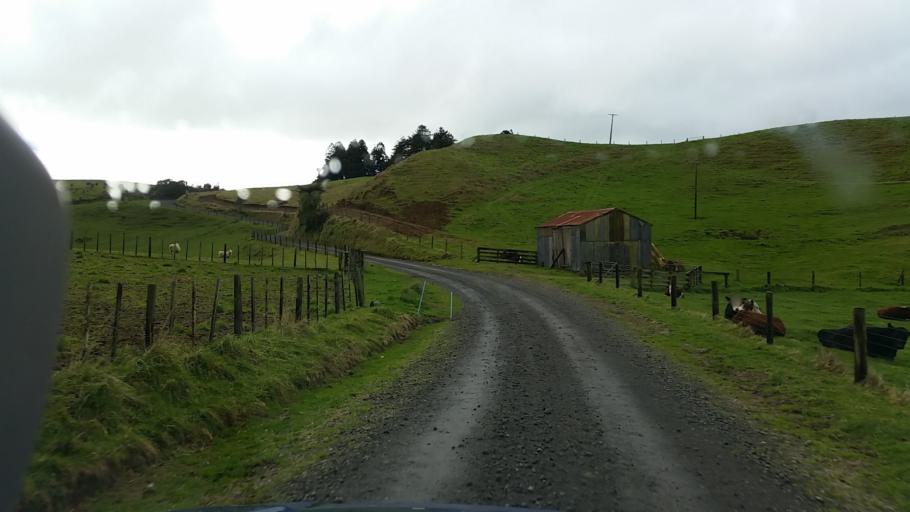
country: NZ
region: Taranaki
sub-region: South Taranaki District
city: Eltham
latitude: -39.2794
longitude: 174.3383
